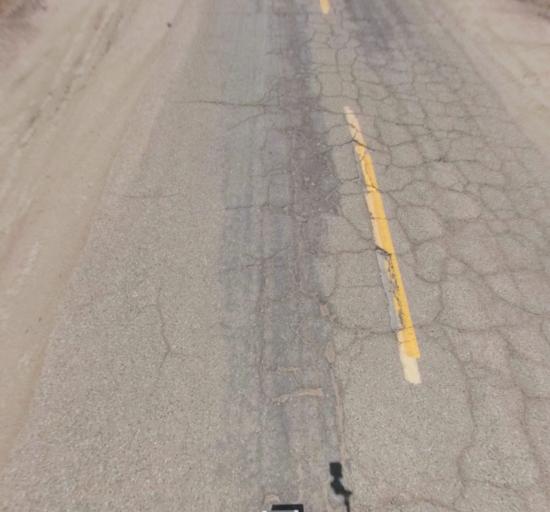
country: US
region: California
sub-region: Madera County
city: Chowchilla
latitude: 37.0617
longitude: -120.2869
